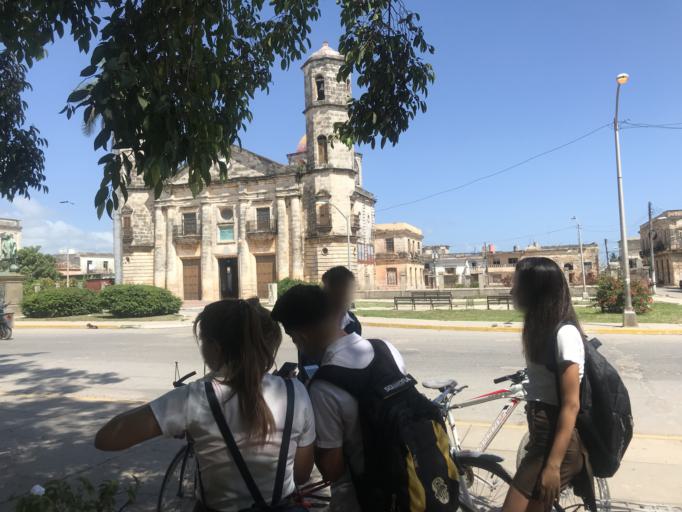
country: CU
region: Matanzas
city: Cardenas
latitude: 23.0413
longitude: -81.2010
